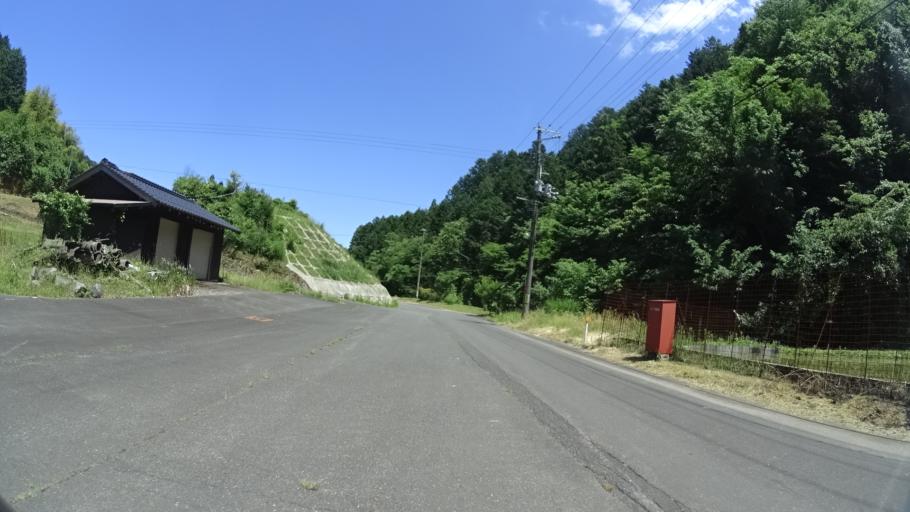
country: JP
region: Kyoto
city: Miyazu
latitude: 35.4406
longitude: 135.1848
